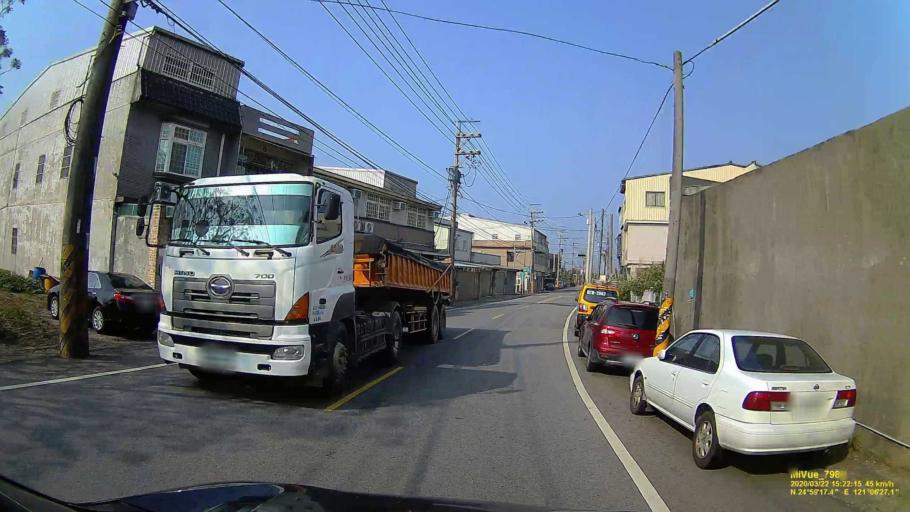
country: TW
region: Taiwan
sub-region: Hsinchu
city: Zhubei
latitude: 24.9884
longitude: 121.1076
